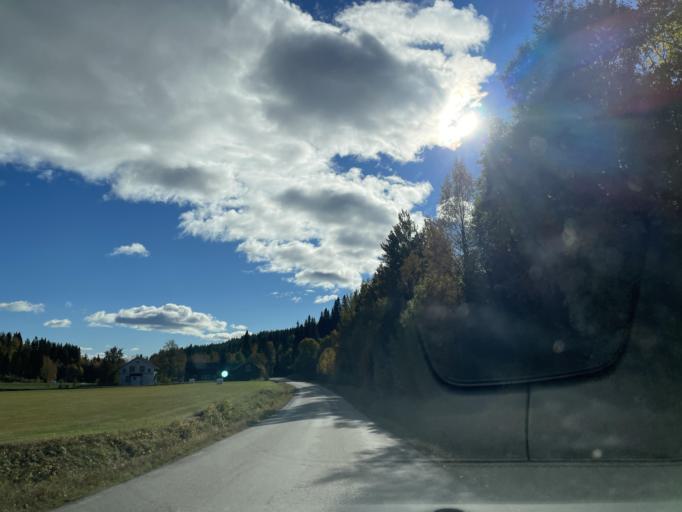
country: SE
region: Dalarna
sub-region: Malung-Saelens kommun
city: Malung
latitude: 61.1422
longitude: 13.2697
